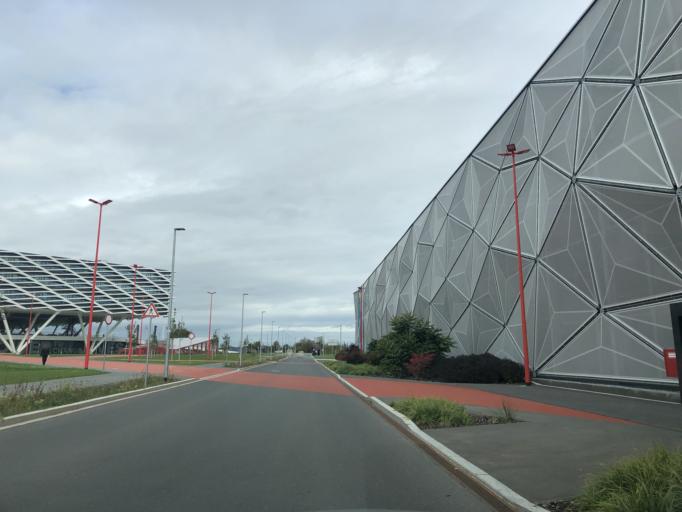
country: DE
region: Bavaria
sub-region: Regierungsbezirk Mittelfranken
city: Herzogenaurach
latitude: 49.5775
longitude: 10.9176
